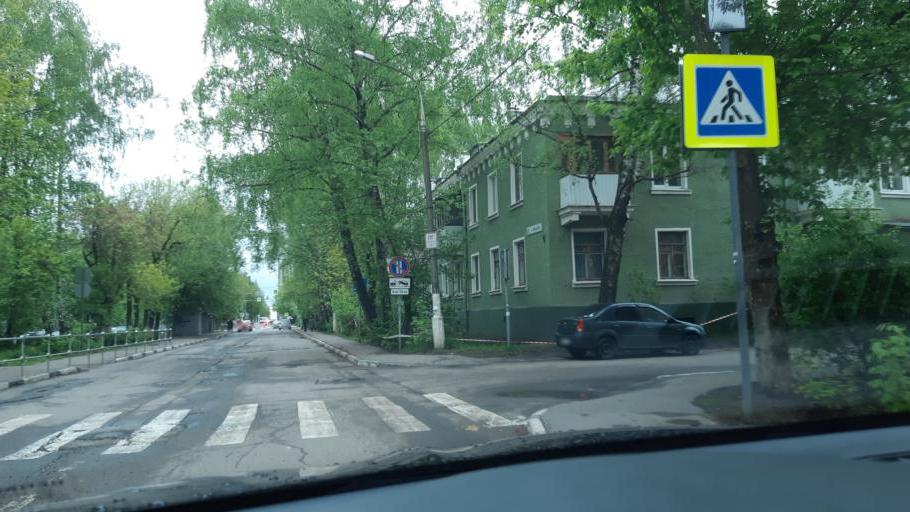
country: RU
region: Moskovskaya
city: Dolgoprudnyy
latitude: 55.9491
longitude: 37.4889
